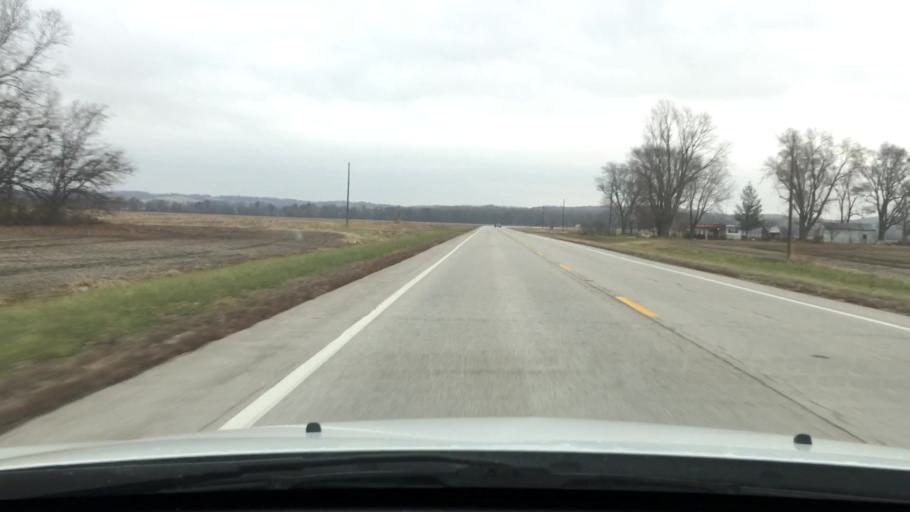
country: US
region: Missouri
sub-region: Pike County
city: Louisiana
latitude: 39.4949
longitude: -91.0041
